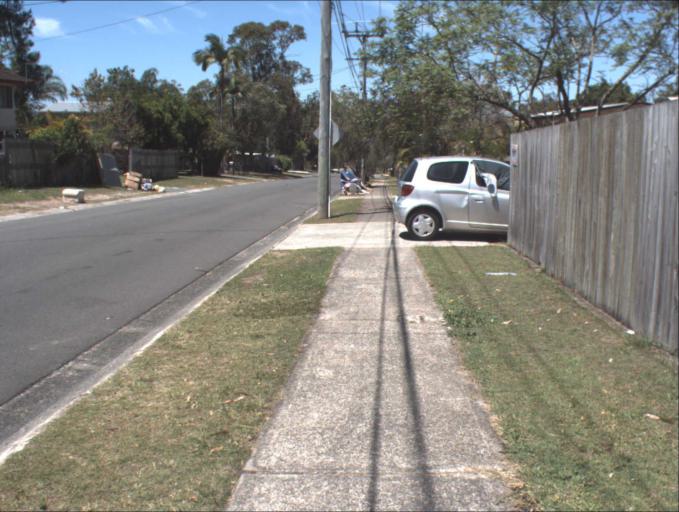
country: AU
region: Queensland
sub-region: Logan
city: Logan City
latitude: -27.6390
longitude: 153.1198
